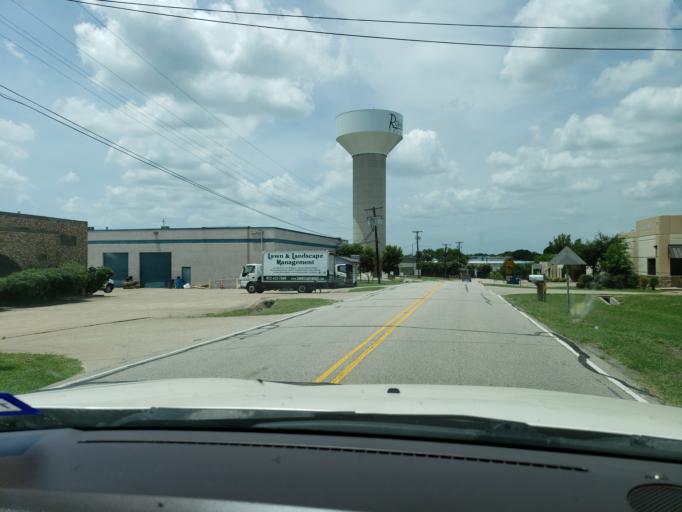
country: US
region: Texas
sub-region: Dallas County
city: Rowlett
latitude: 32.9025
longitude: -96.5709
